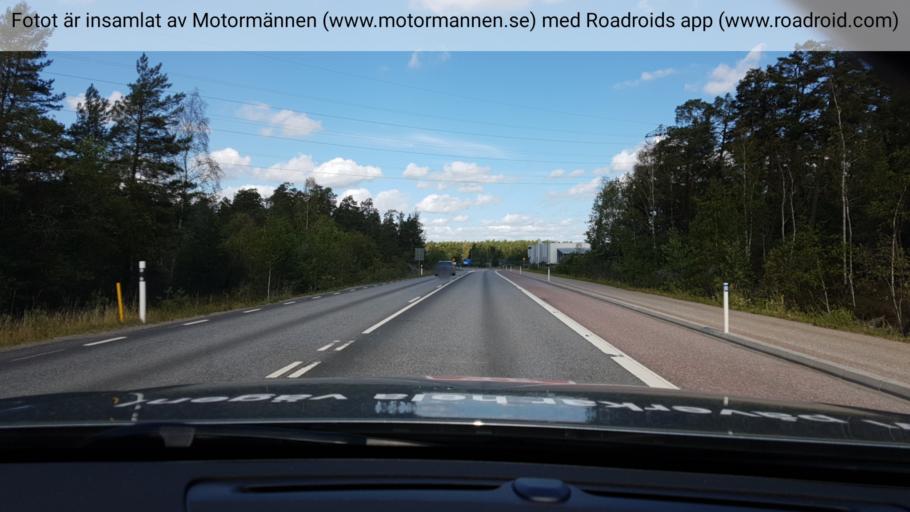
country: SE
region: Soedermanland
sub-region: Strangnas Kommun
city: Strangnas
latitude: 59.3715
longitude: 17.0056
